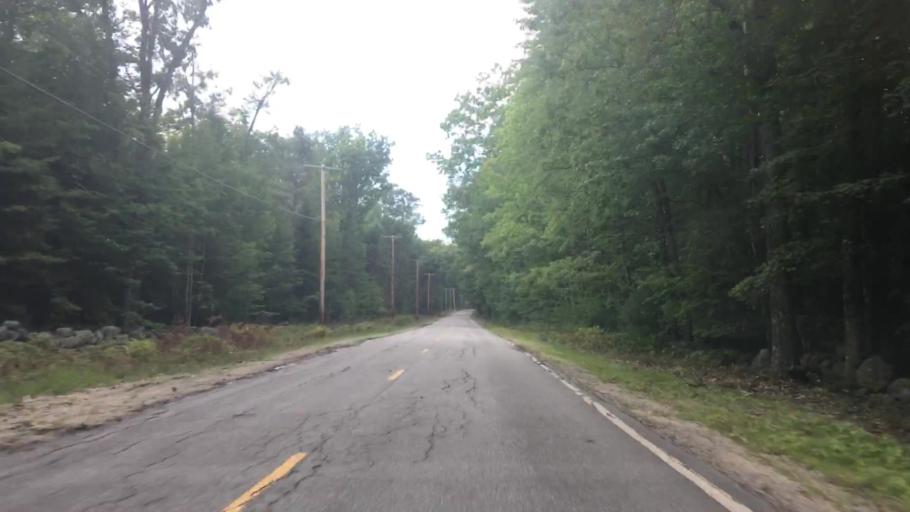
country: US
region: Maine
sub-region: Oxford County
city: Oxford
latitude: 44.0360
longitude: -70.5361
